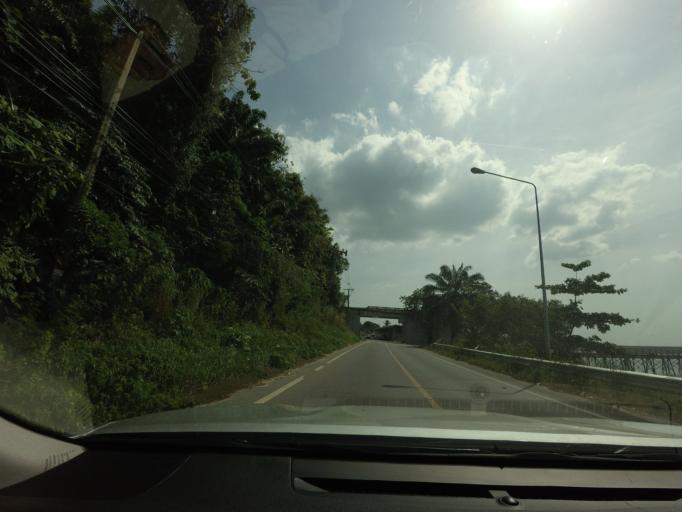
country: TH
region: Phangnga
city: Ban Ao Nang
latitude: 8.0690
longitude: 98.7444
